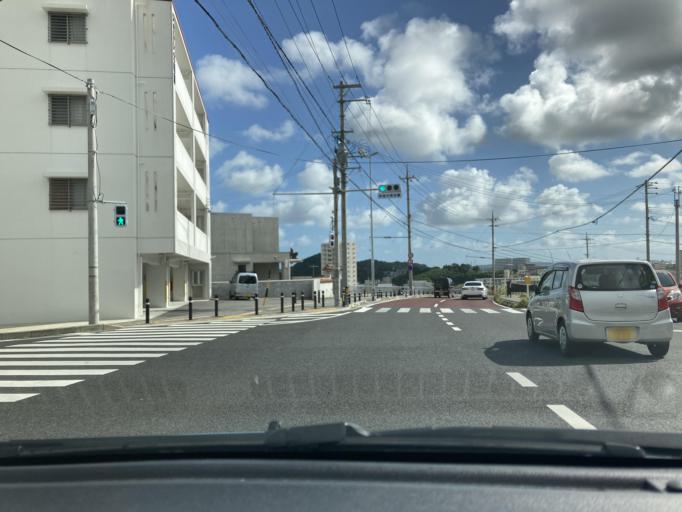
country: JP
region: Okinawa
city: Tomigusuku
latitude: 26.2001
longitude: 127.7298
